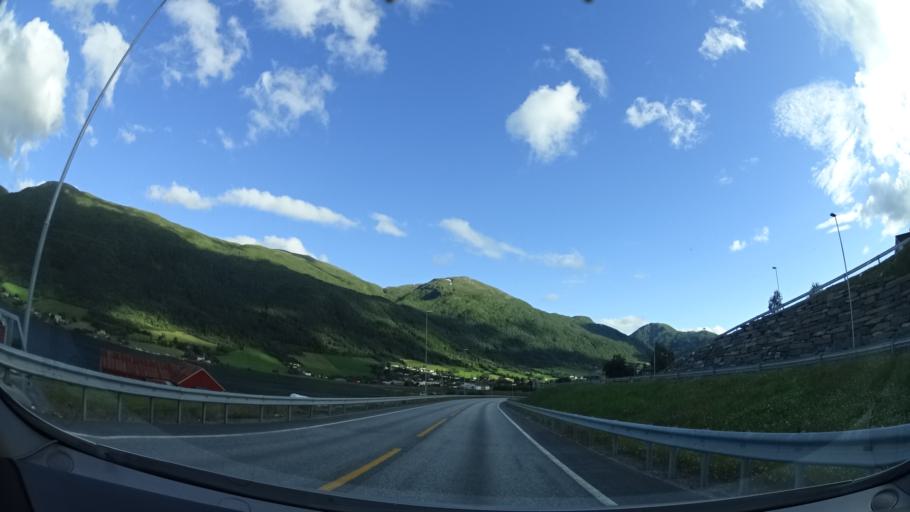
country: NO
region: More og Romsdal
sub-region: Gjemnes
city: Batnfjordsora
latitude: 62.9018
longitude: 7.6757
